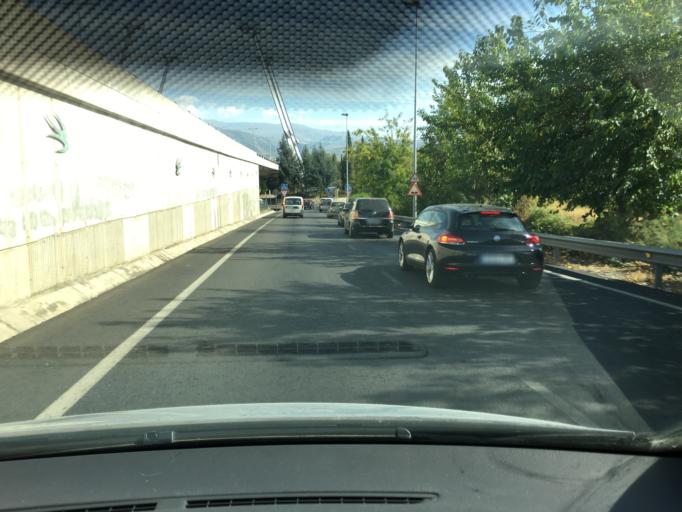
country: ES
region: Andalusia
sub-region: Provincia de Granada
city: Granada
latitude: 37.1772
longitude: -3.6152
